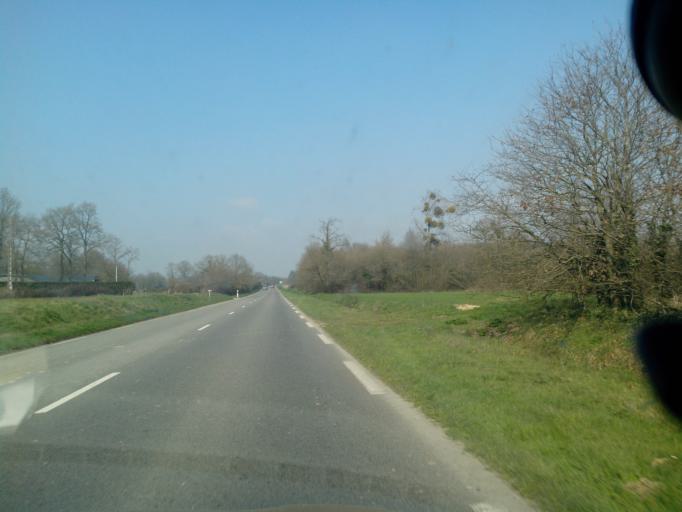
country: FR
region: Brittany
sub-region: Departement d'Ille-et-Vilaine
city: Saint-Meen-le-Grand
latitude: 48.2165
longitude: -2.1768
